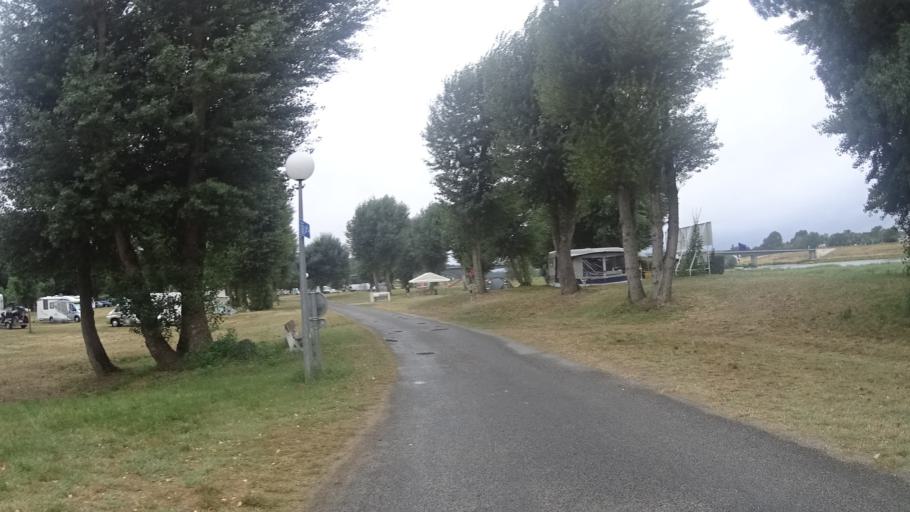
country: FR
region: Centre
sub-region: Departement du Loir-et-Cher
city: Chaumont-sur-Loire
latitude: 47.4861
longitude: 1.1957
